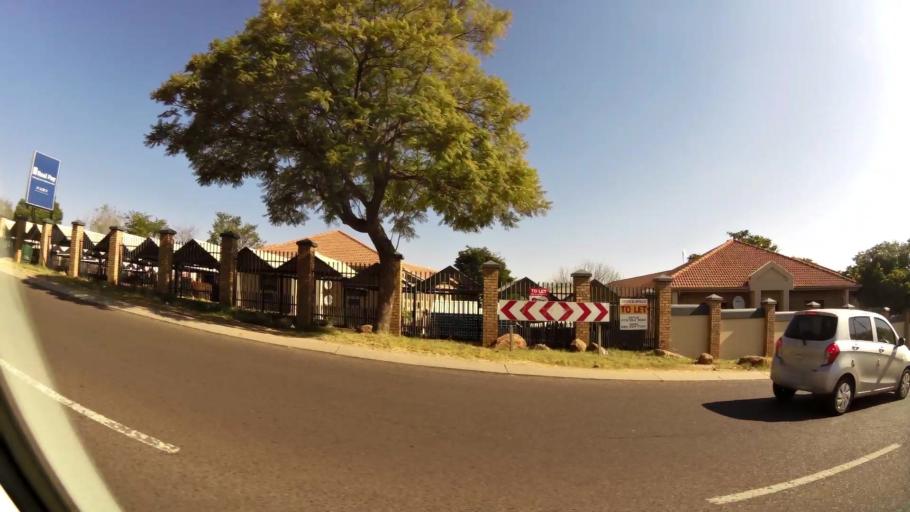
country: ZA
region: Gauteng
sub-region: City of Tshwane Metropolitan Municipality
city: Centurion
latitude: -25.8180
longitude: 28.2706
